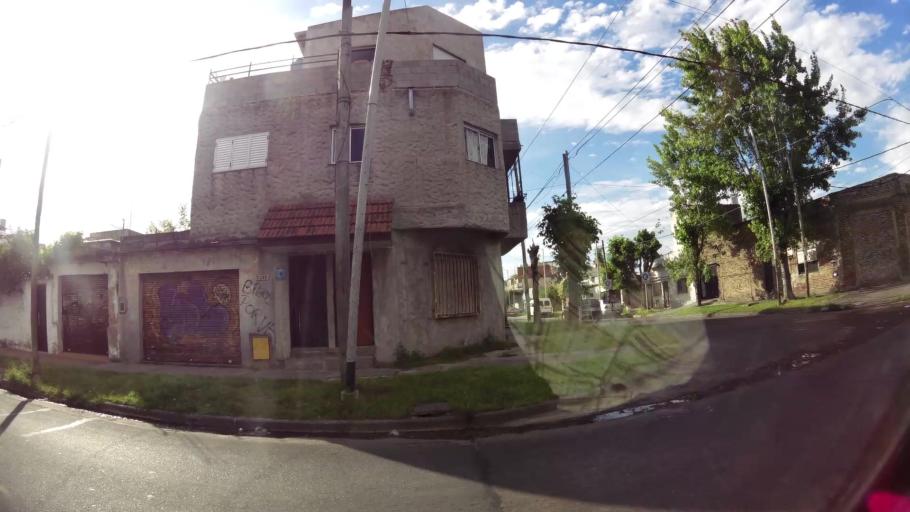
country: AR
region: Buenos Aires
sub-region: Partido de Lanus
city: Lanus
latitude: -34.6930
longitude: -58.3716
